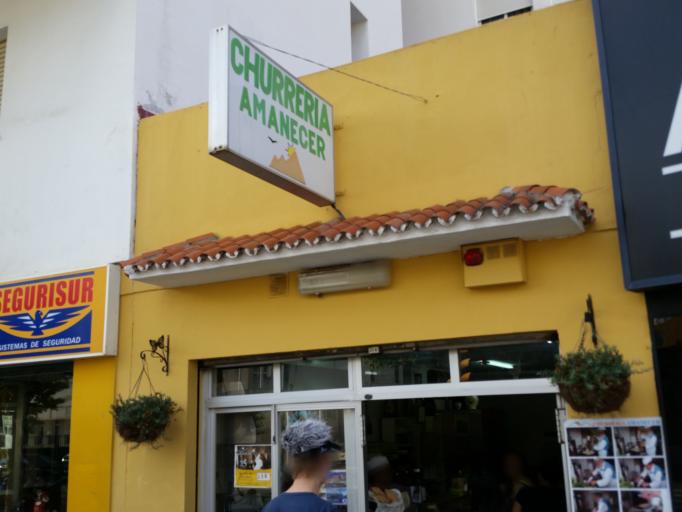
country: ES
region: Andalusia
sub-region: Provincia de Malaga
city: Torremolinos
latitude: 36.6005
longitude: -4.5287
